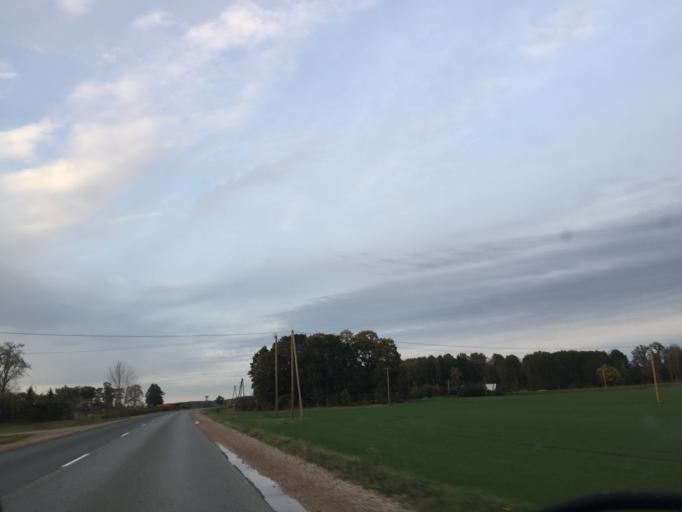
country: LV
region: Dobeles Rajons
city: Dobele
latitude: 56.7236
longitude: 23.3872
